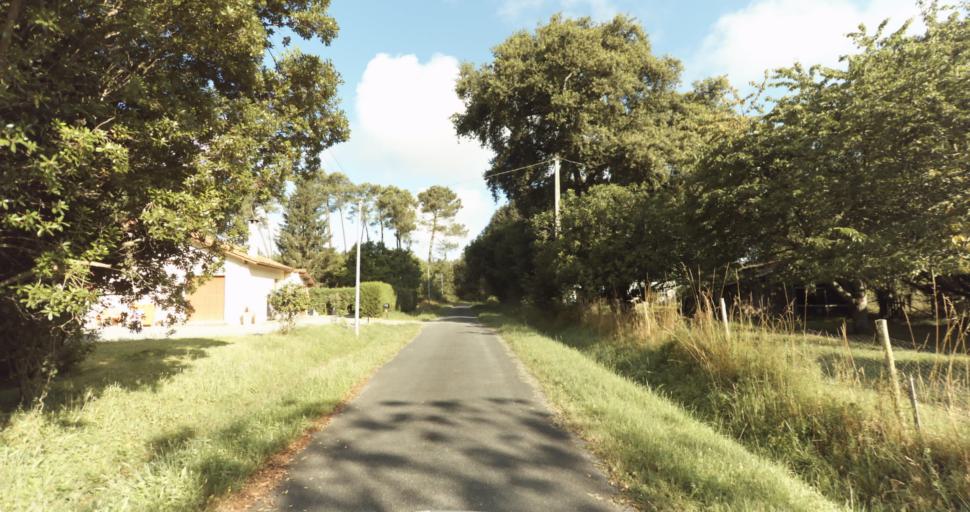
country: FR
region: Aquitaine
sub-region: Departement de la Gironde
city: Bazas
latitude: 44.4430
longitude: -0.2491
